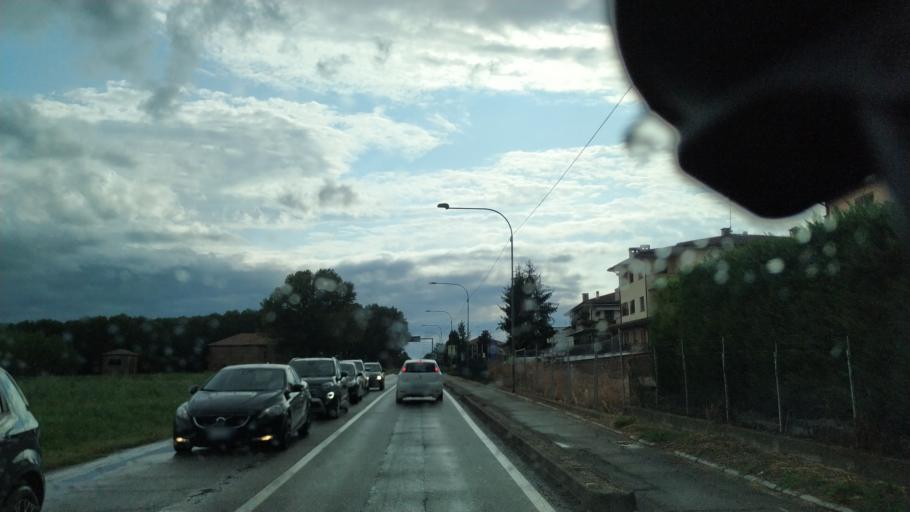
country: IT
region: Emilia-Romagna
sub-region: Provincia di Ferrara
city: Mirabello
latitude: 44.8193
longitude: 11.4520
